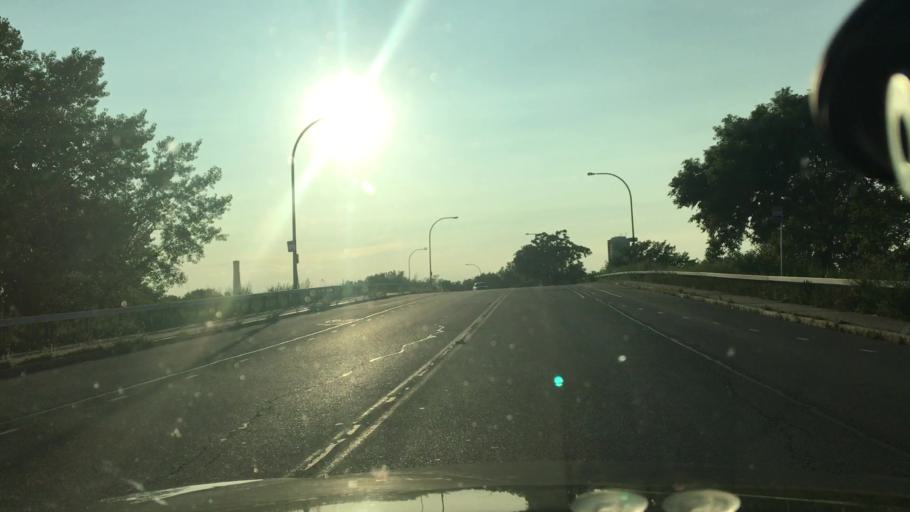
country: US
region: New York
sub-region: Erie County
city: Buffalo
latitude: 42.8695
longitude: -78.8530
